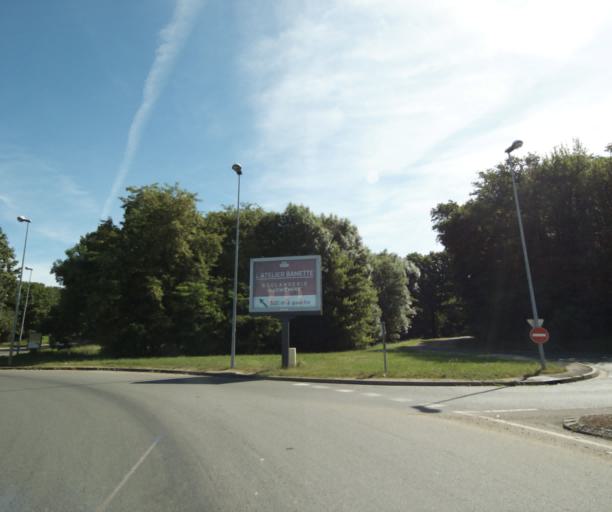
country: FR
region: Centre
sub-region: Departement d'Eure-et-Loir
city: Luce
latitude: 48.4210
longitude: 1.4505
